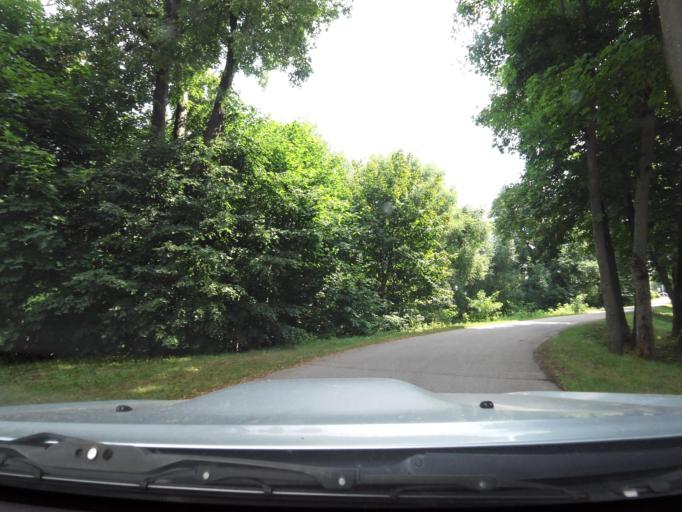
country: RU
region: Kaliningrad
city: Sovetsk
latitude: 55.0874
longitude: 21.9077
